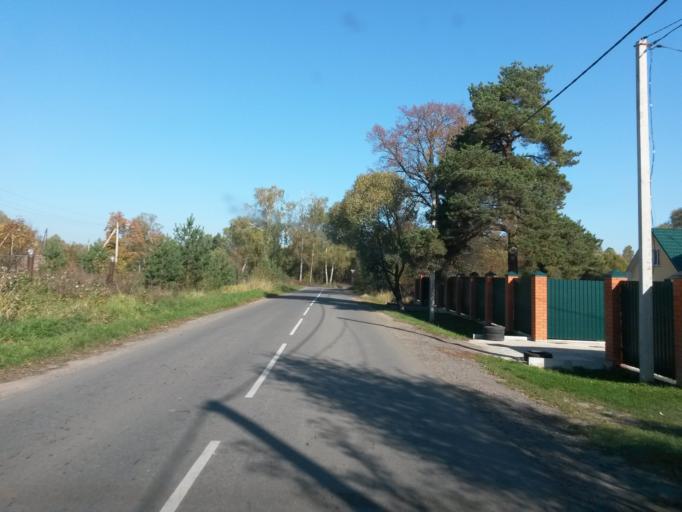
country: RU
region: Moskovskaya
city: Lyubuchany
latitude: 55.2490
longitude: 37.6168
